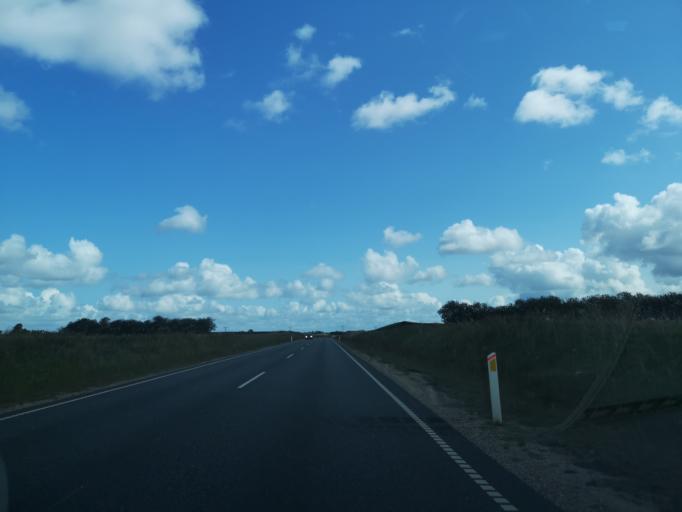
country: DK
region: Central Jutland
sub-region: Holstebro Kommune
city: Holstebro
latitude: 56.3931
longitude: 8.5594
